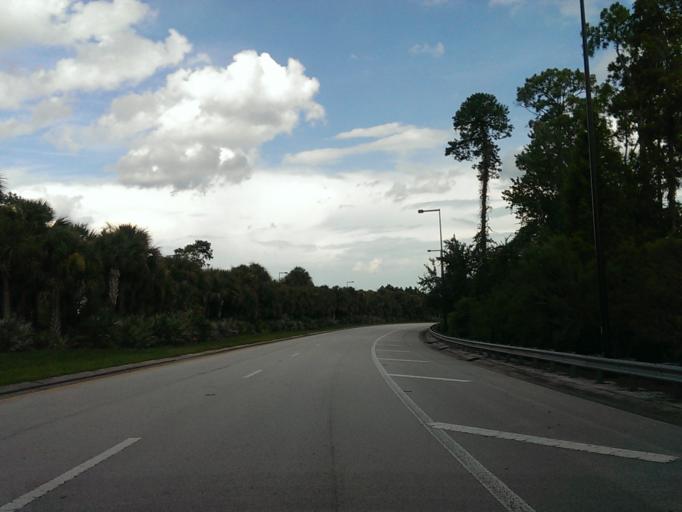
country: US
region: Florida
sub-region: Polk County
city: Citrus Ridge
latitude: 28.3778
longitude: -81.6028
